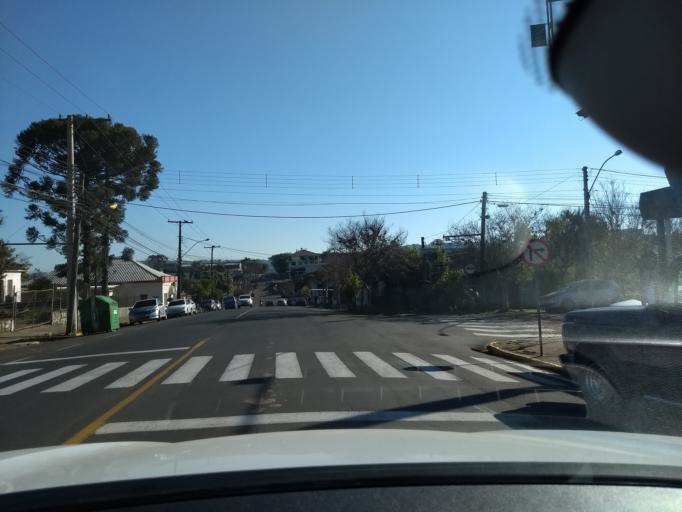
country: BR
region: Rio Grande do Sul
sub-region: Santa Cruz Do Sul
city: Santa Cruz do Sul
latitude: -29.7184
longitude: -52.4415
